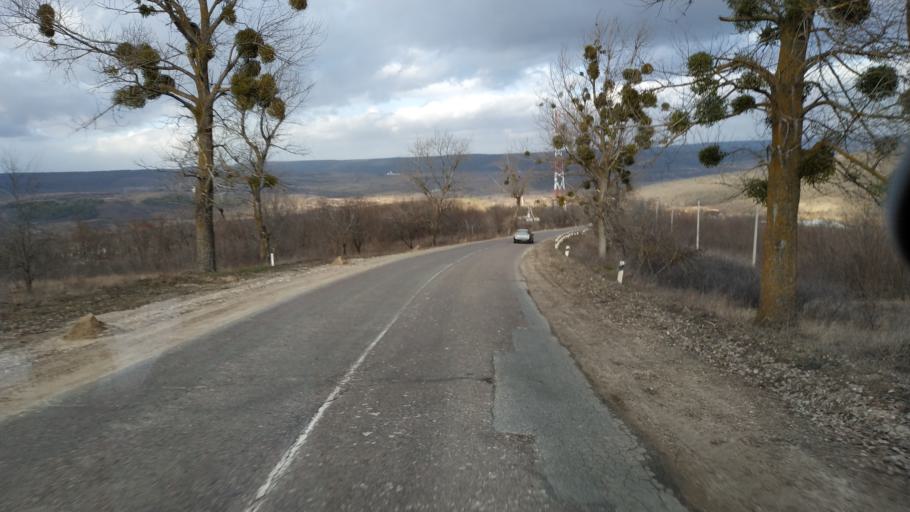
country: MD
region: Calarasi
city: Calarasi
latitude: 47.2964
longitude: 28.3624
